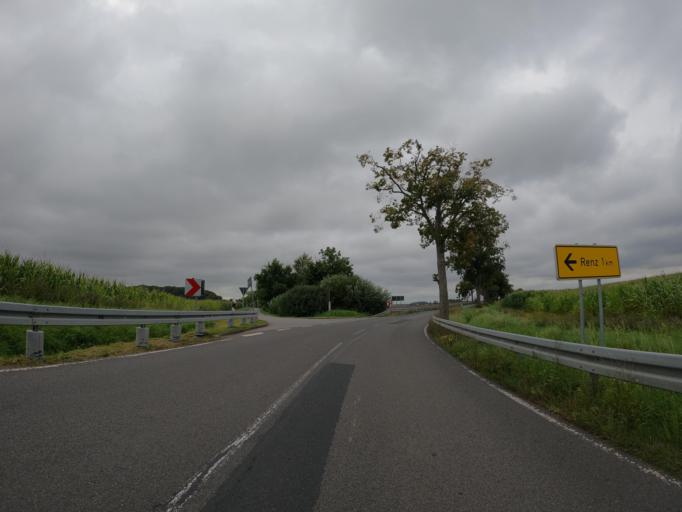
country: DE
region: Mecklenburg-Vorpommern
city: Garz
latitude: 54.3122
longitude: 13.3344
